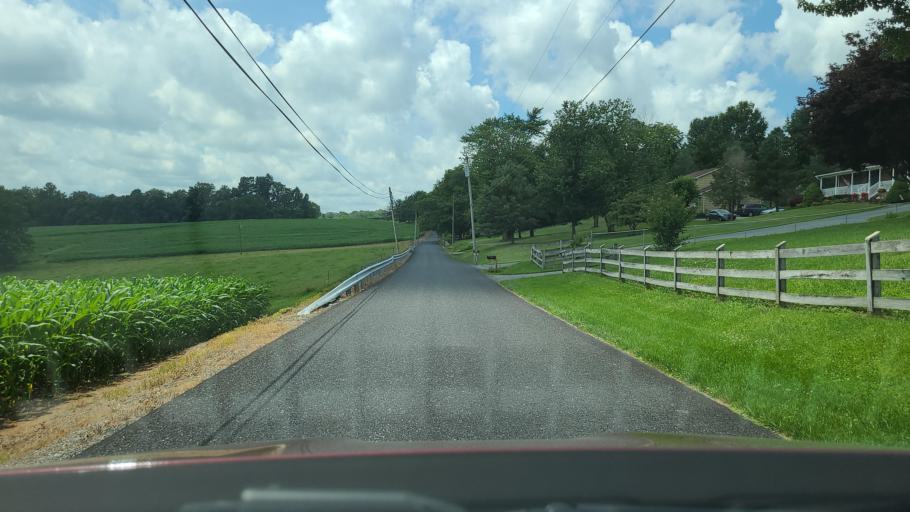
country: US
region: Maryland
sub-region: Carroll County
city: Westminster
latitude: 39.5444
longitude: -77.0245
